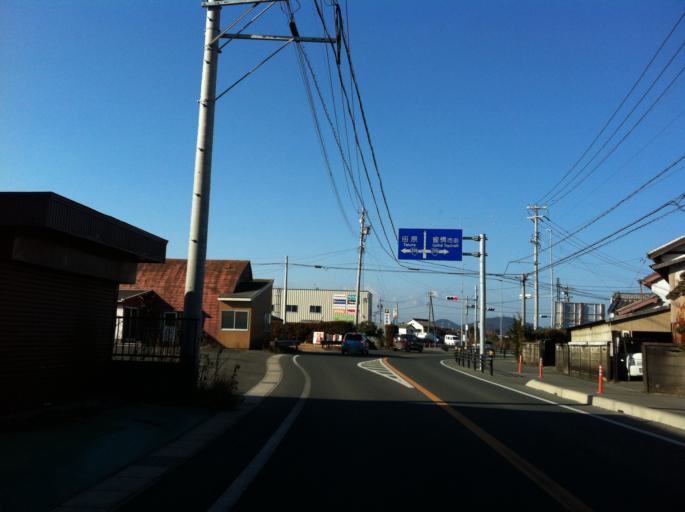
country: JP
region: Aichi
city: Tahara
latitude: 34.6918
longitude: 137.3296
